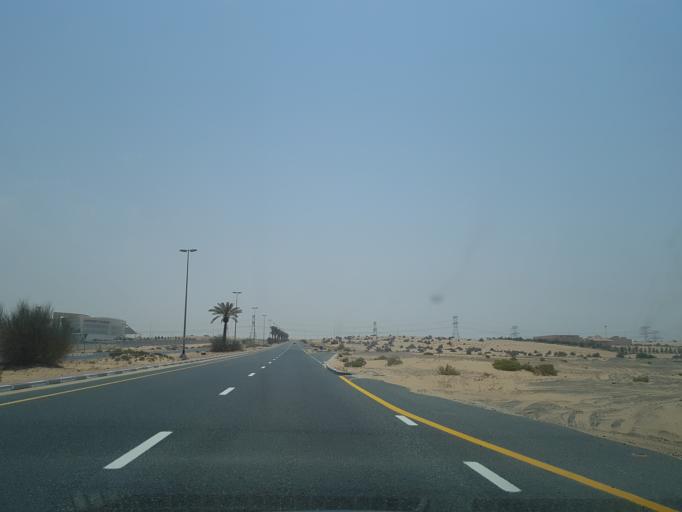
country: AE
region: Ash Shariqah
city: Sharjah
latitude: 25.1093
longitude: 55.4094
